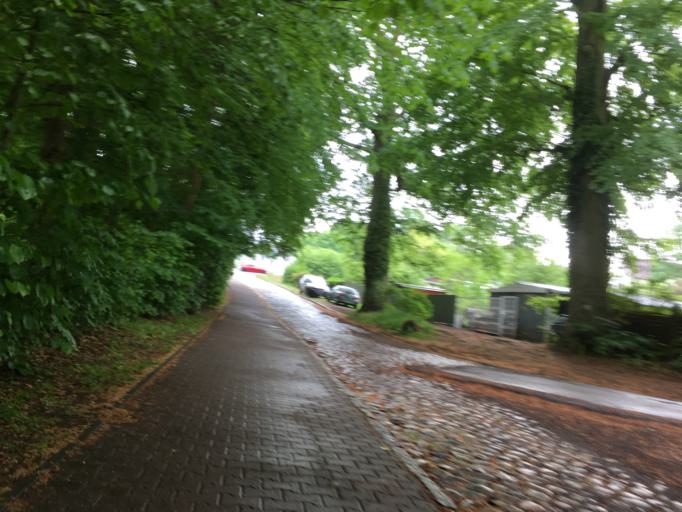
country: DE
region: Brandenburg
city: Eberswalde
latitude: 52.8408
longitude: 13.7859
